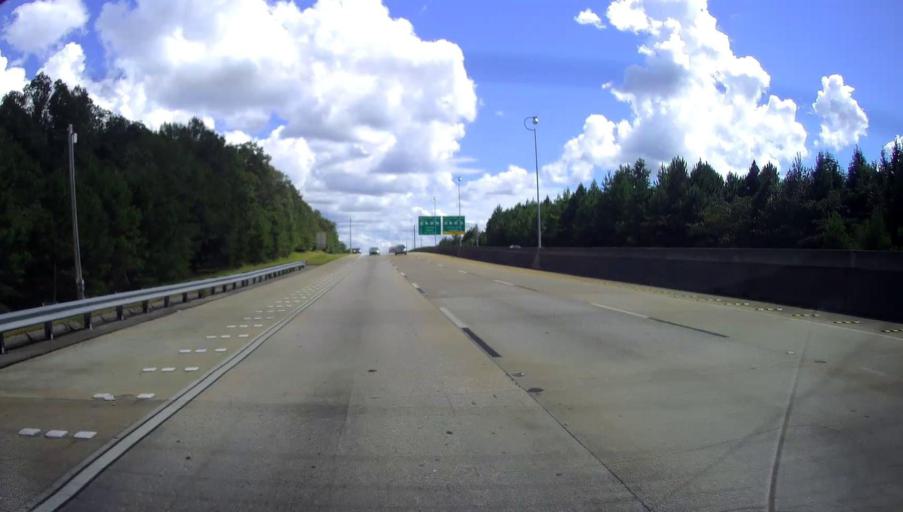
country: US
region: Georgia
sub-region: Muscogee County
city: Columbus
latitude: 32.4185
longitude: -84.9276
